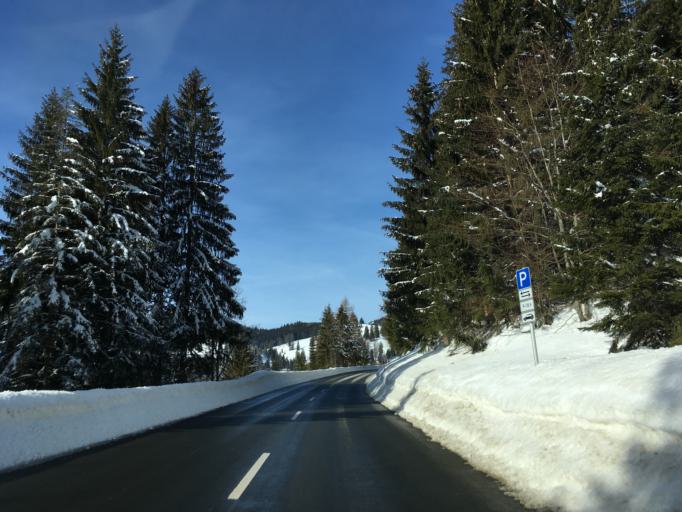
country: DE
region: Bavaria
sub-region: Upper Bavaria
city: Bayrischzell
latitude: 47.6818
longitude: 12.0499
